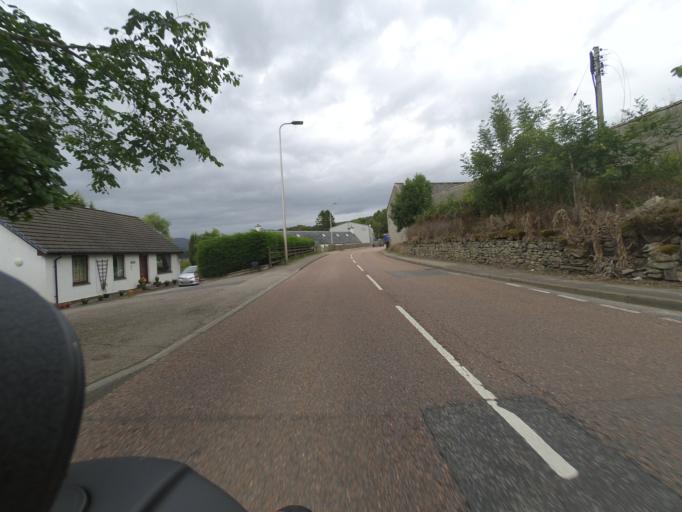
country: GB
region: Scotland
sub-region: Highland
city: Muir of Ord
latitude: 57.5666
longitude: -4.5790
